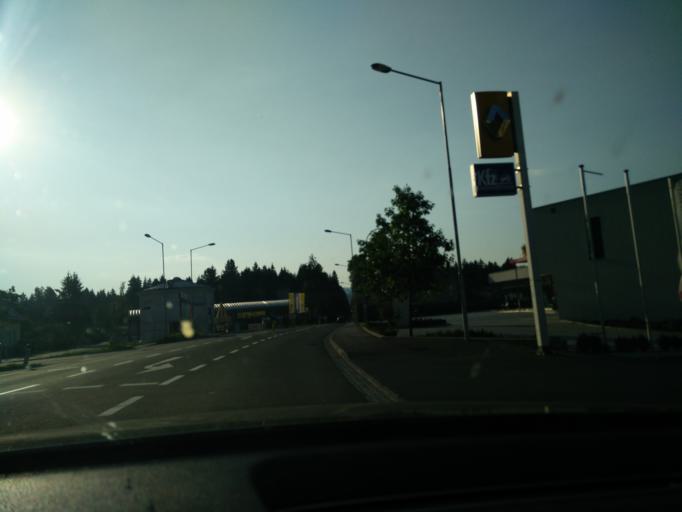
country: AT
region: Carinthia
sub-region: Politischer Bezirk Klagenfurt Land
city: Ferlach
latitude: 46.5283
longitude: 14.2912
